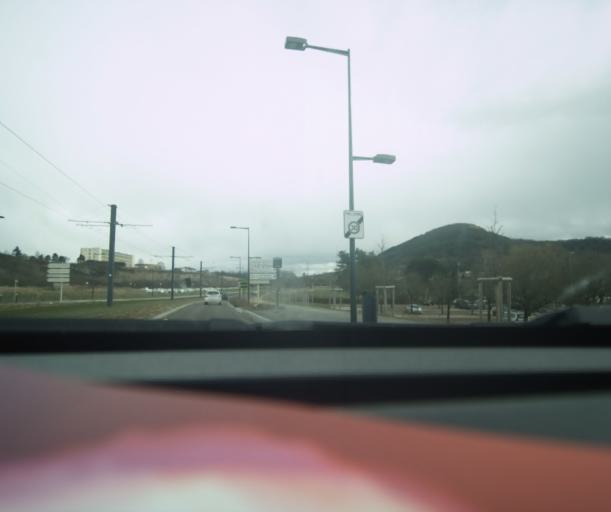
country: FR
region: Franche-Comte
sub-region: Departement du Doubs
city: Beure
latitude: 47.2226
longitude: 5.9829
